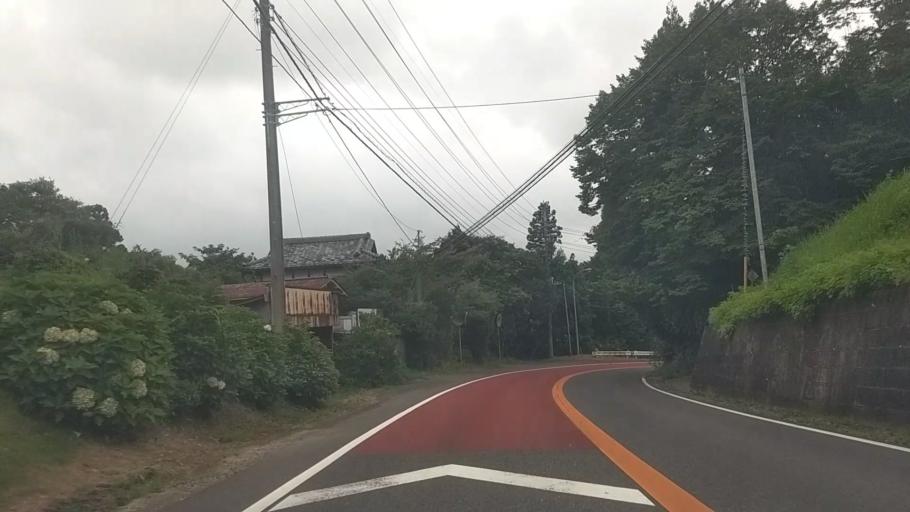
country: JP
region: Chiba
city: Kawaguchi
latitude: 35.2257
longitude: 140.0744
